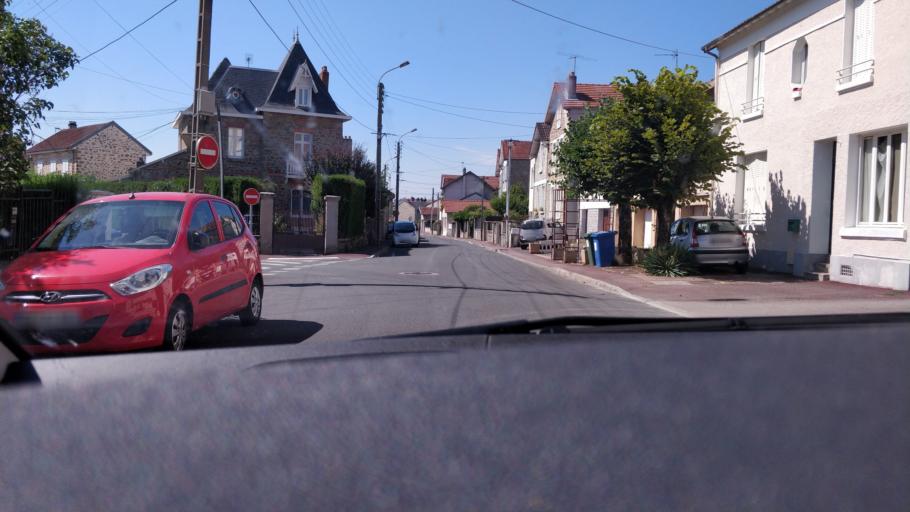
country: FR
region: Limousin
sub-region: Departement de la Haute-Vienne
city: Limoges
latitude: 45.8474
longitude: 1.2479
